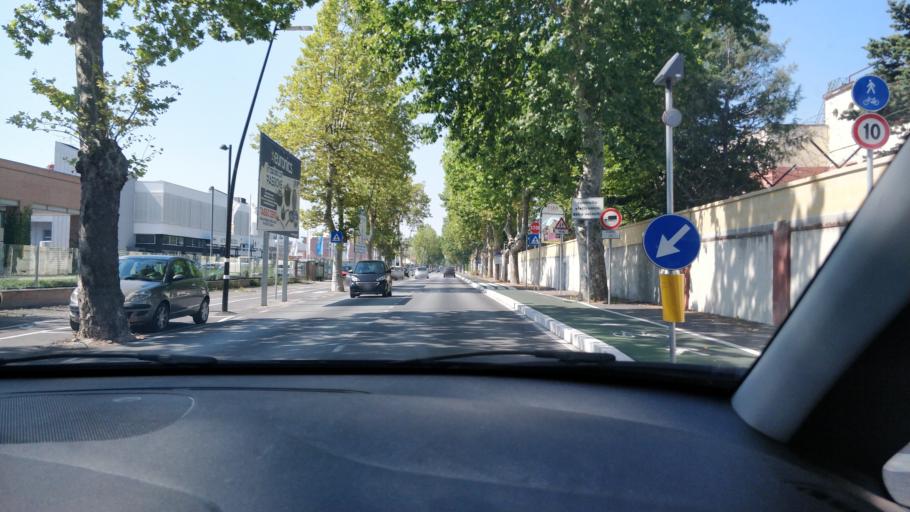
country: IT
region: Abruzzo
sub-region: Provincia di Chieti
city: Sambuceto
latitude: 42.4368
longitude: 14.1941
